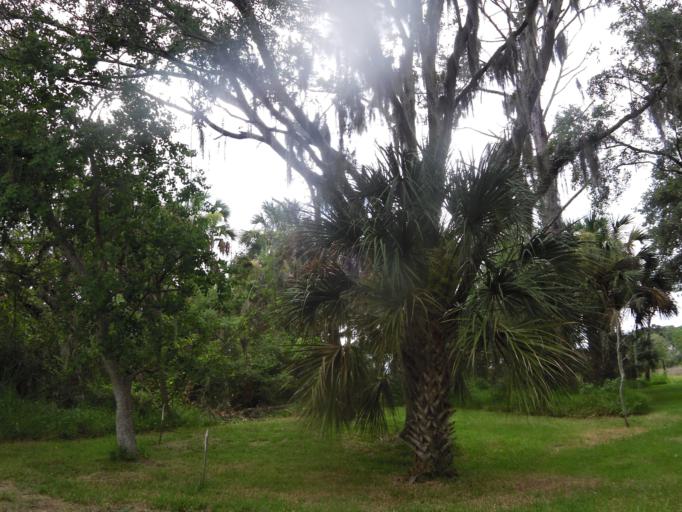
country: US
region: Florida
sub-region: Duval County
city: Atlantic Beach
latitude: 30.3341
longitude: -81.4266
